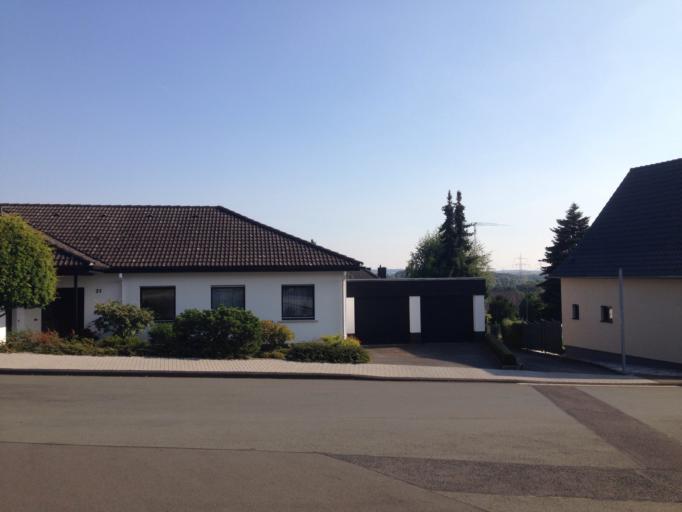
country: DE
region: Hesse
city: Allendorf an der Lahn
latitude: 50.5538
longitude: 8.6241
